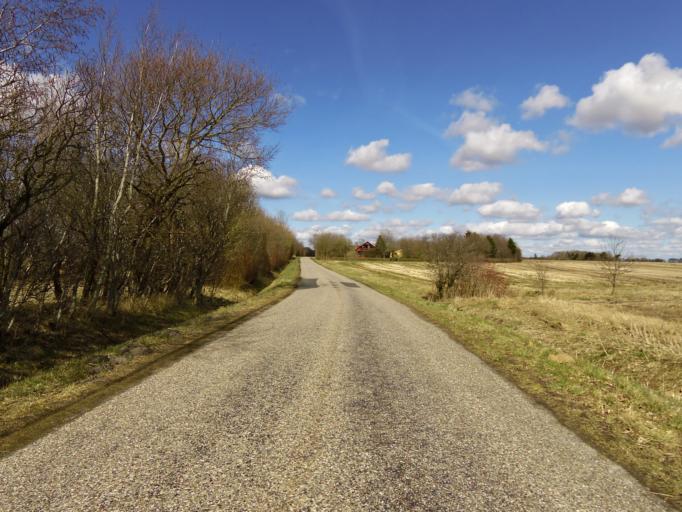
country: DK
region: South Denmark
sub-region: Tonder Kommune
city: Toftlund
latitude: 55.1735
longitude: 9.0878
